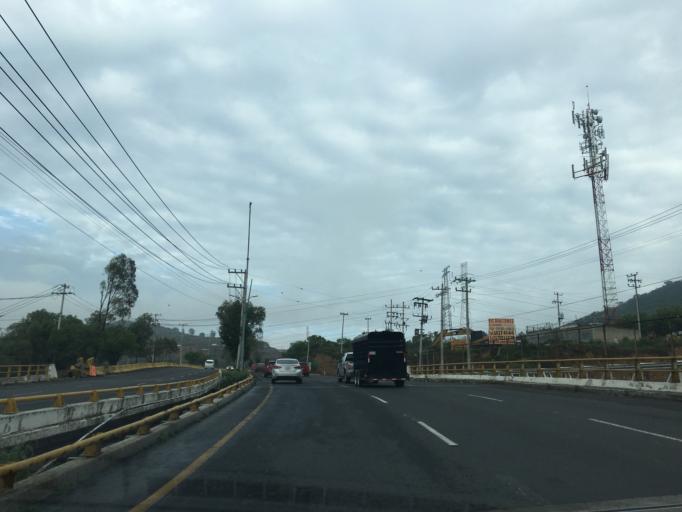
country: MX
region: Mexico
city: Ciudad Lopez Mateos
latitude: 19.5463
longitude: -99.2767
